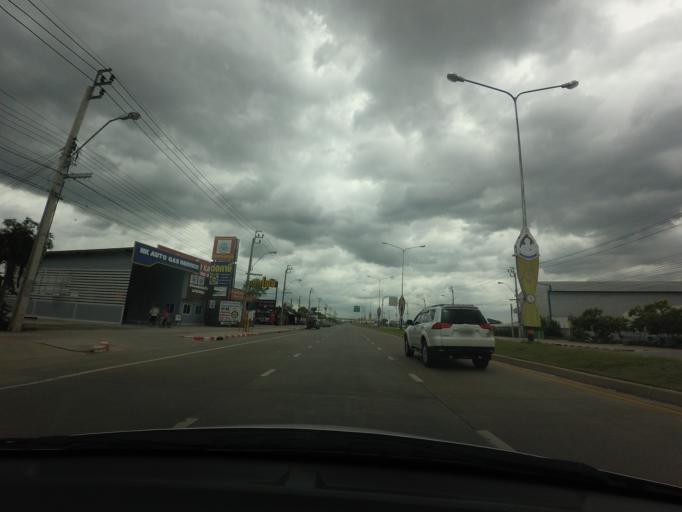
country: TH
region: Bangkok
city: Saphan Sung
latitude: 13.7542
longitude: 100.7165
